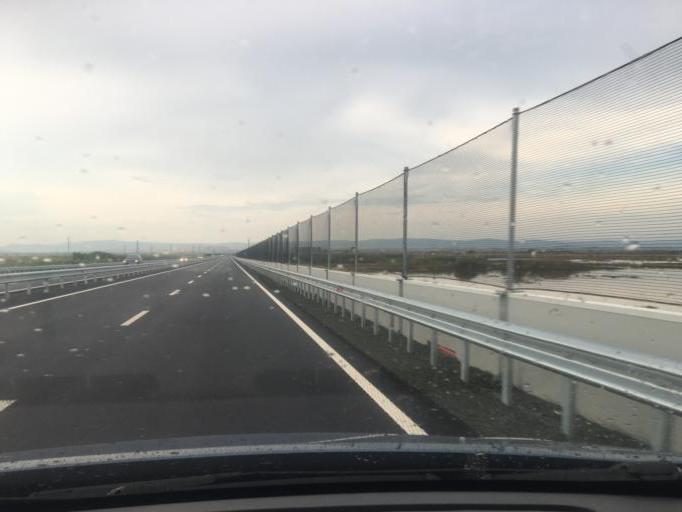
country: BG
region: Burgas
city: Aheloy
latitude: 42.6102
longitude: 27.6221
